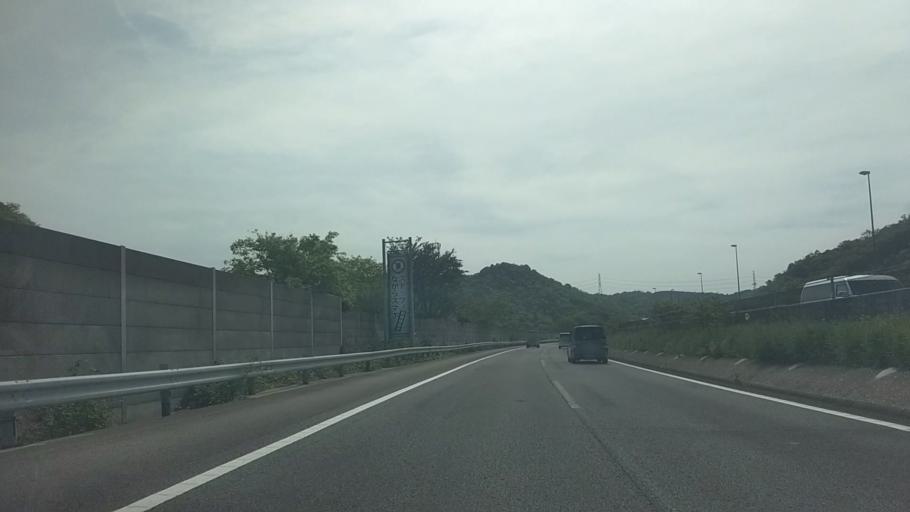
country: JP
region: Aichi
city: Okazaki
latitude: 34.9227
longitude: 137.2321
